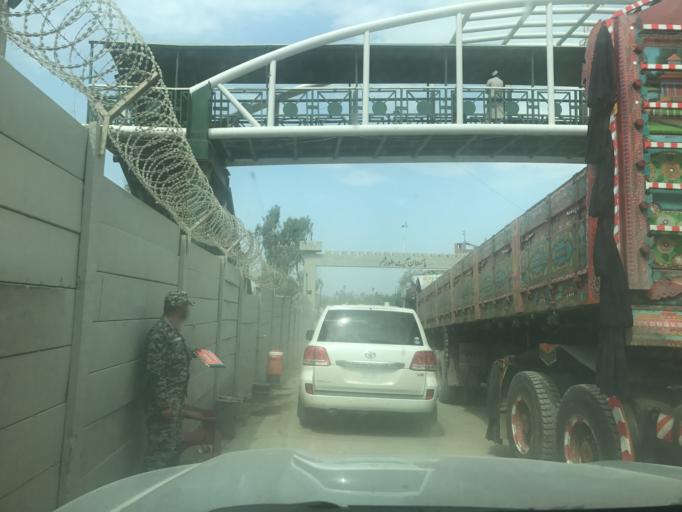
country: PK
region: Federally Administered Tribal Areas
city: Landi Kotal
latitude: 34.1210
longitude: 71.0950
